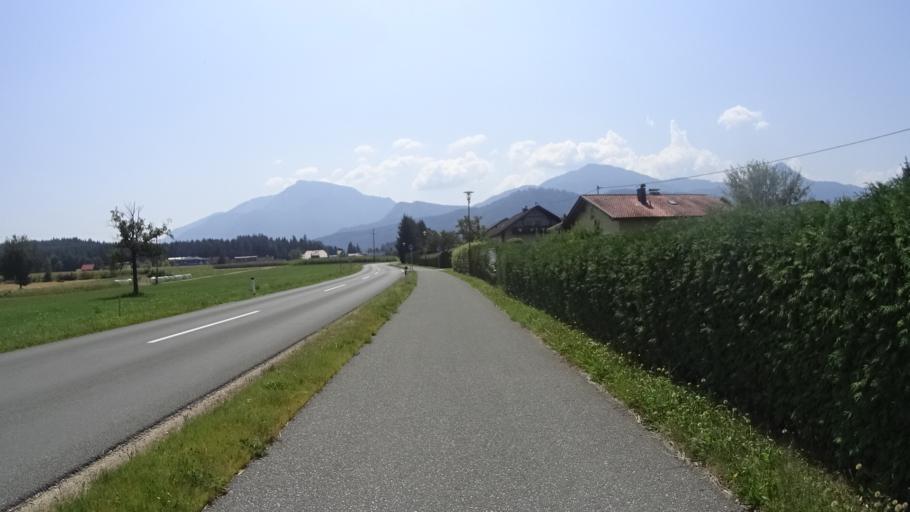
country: AT
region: Carinthia
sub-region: Politischer Bezirk Volkermarkt
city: Eberndorf
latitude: 46.5777
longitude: 14.6538
